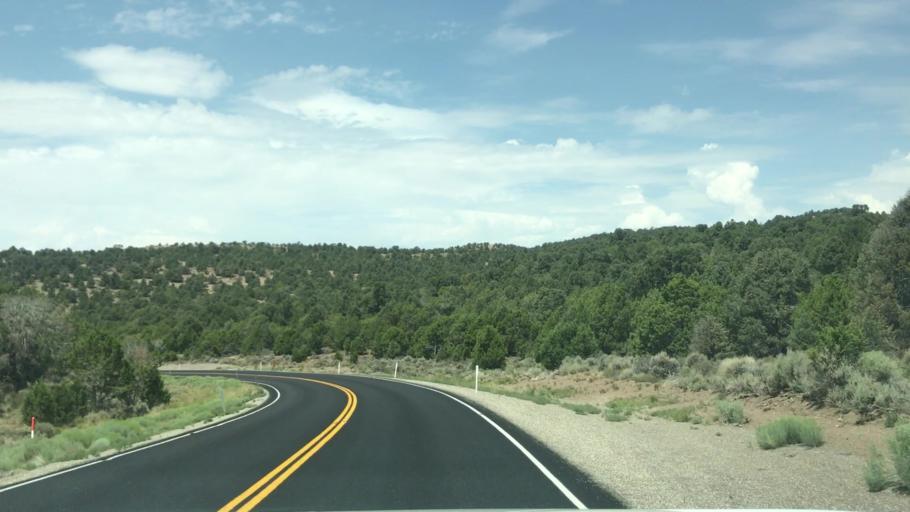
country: US
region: Nevada
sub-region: Eureka County
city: Eureka
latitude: 39.3984
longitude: -115.4721
